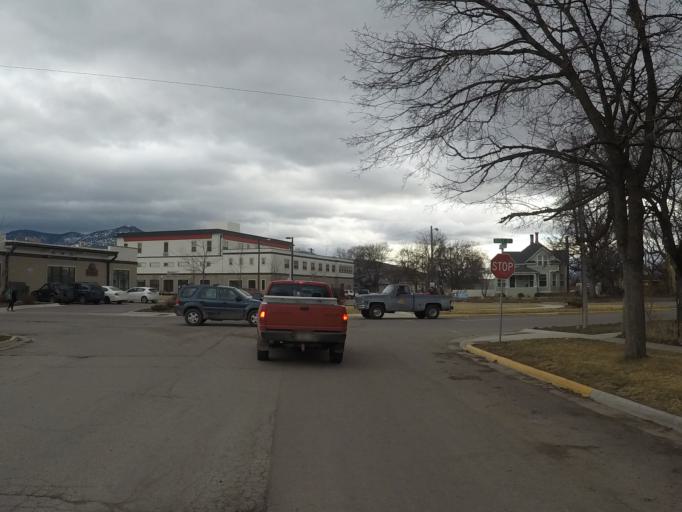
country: US
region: Montana
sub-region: Missoula County
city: Missoula
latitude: 46.8783
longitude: -114.0048
